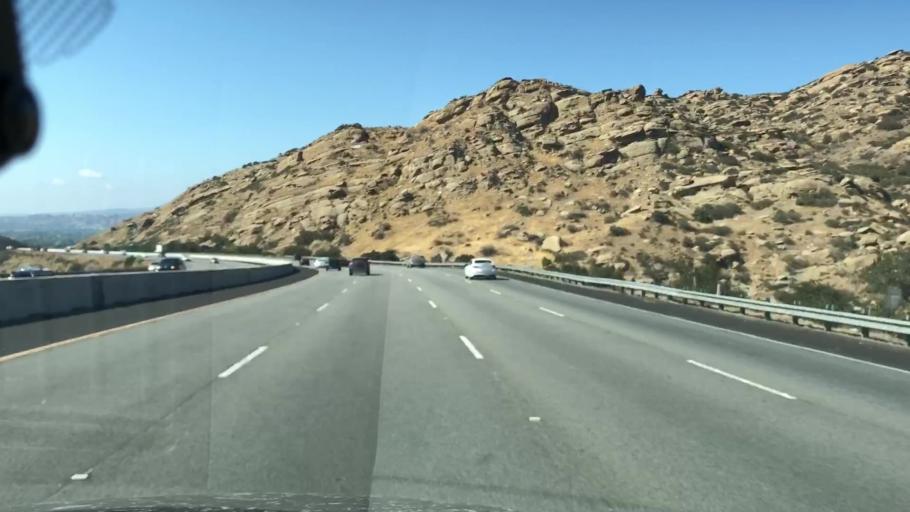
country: US
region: California
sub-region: Los Angeles County
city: Chatsworth
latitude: 34.2687
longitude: -118.6456
